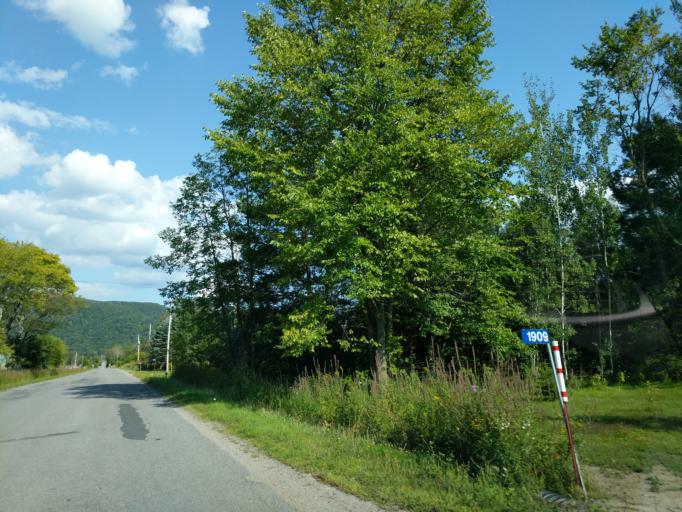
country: CA
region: Quebec
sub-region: Outaouais
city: Wakefield
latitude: 45.5038
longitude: -75.9426
